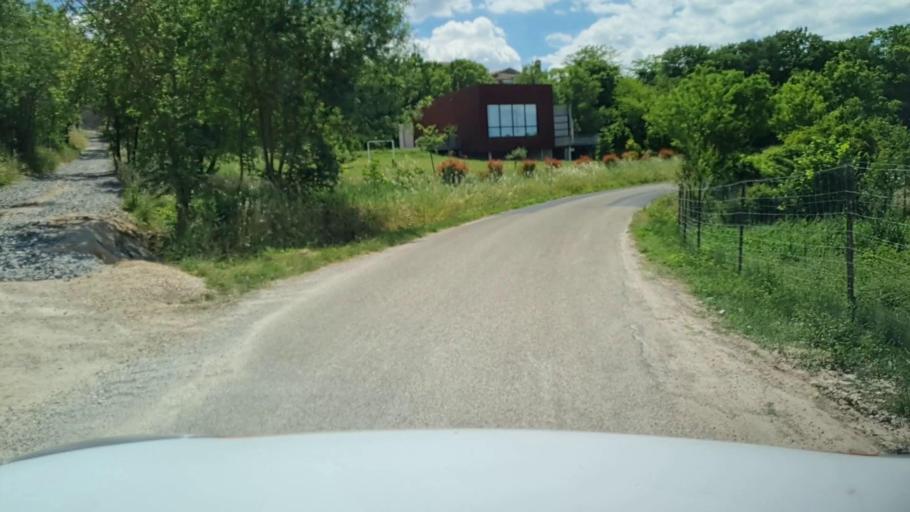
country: FR
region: Languedoc-Roussillon
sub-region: Departement du Gard
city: Saint-Mamert-du-Gard
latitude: 43.8986
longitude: 4.2171
